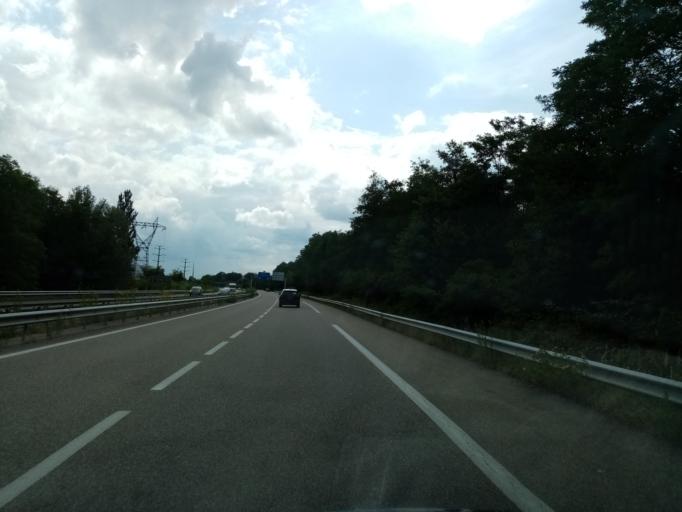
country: FR
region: Alsace
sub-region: Departement du Bas-Rhin
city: Seltz
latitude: 48.8997
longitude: 8.0894
